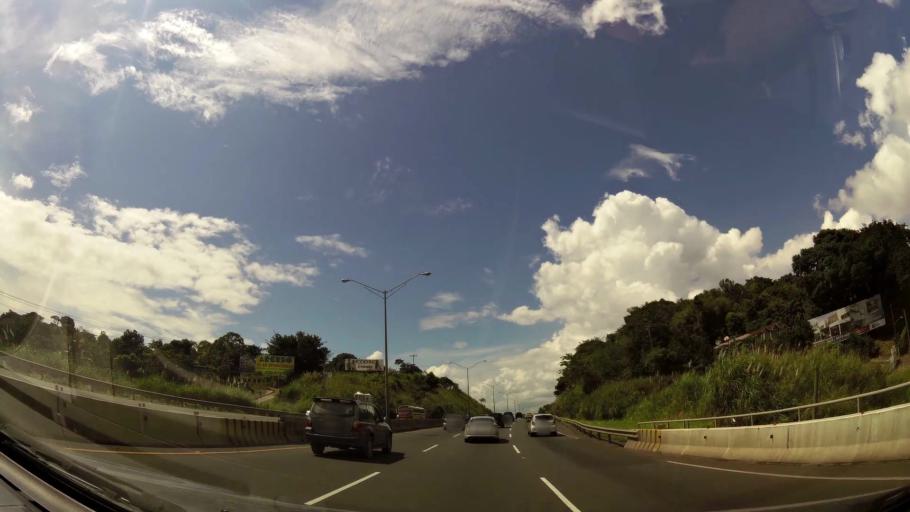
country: PA
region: Panama
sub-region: Distrito Arraijan
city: Arraijan
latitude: 8.9453
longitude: -79.6683
